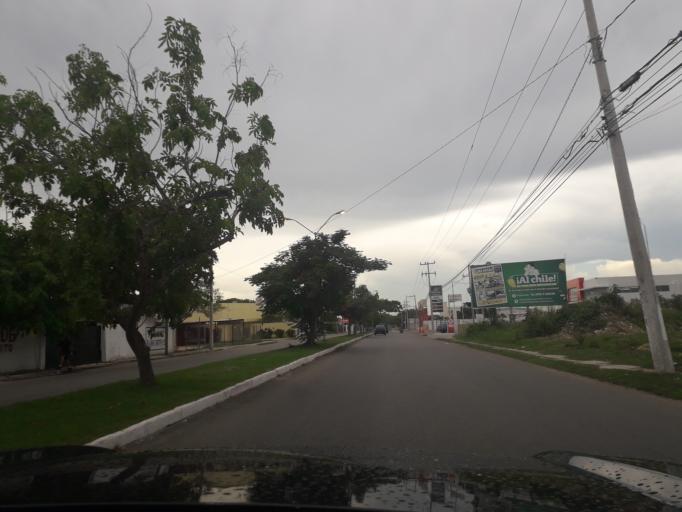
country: MX
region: Yucatan
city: Merida
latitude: 20.9422
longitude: -89.6483
